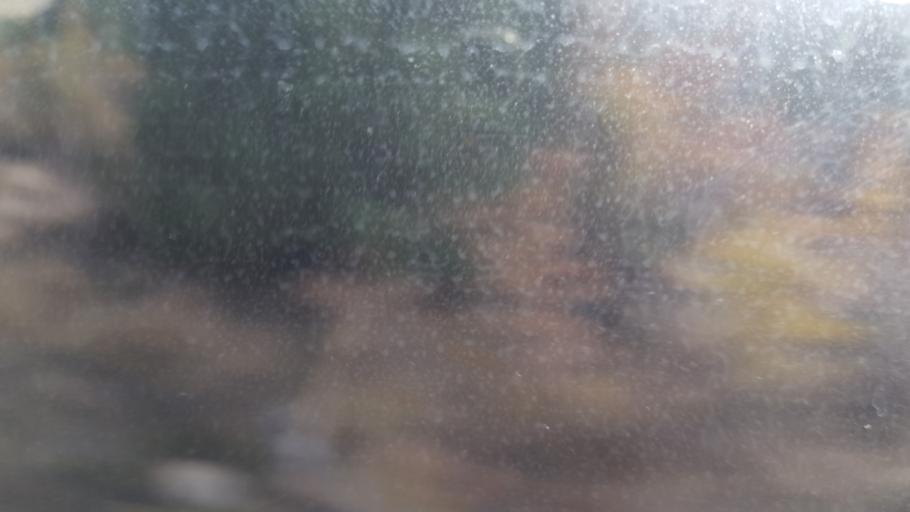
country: TR
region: Ankara
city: Nallihan
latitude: 40.0515
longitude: 31.4003
